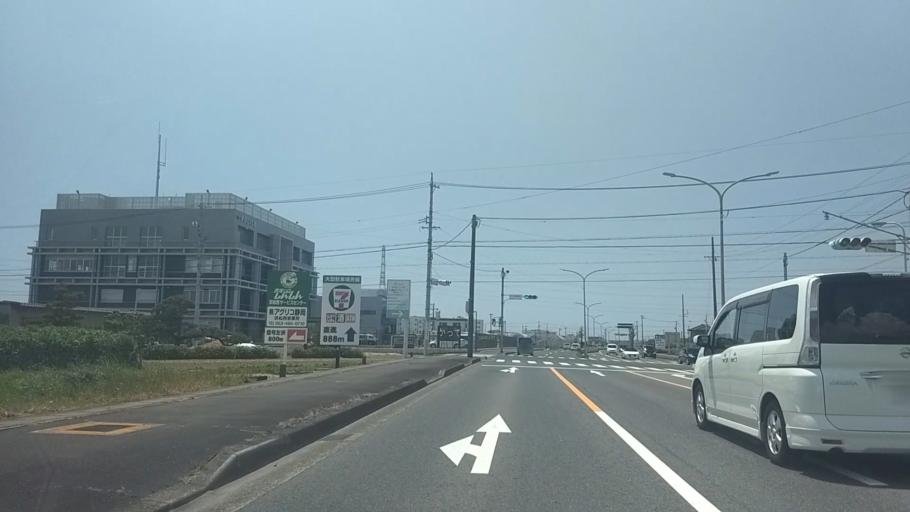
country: JP
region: Shizuoka
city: Hamamatsu
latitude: 34.7372
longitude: 137.6641
